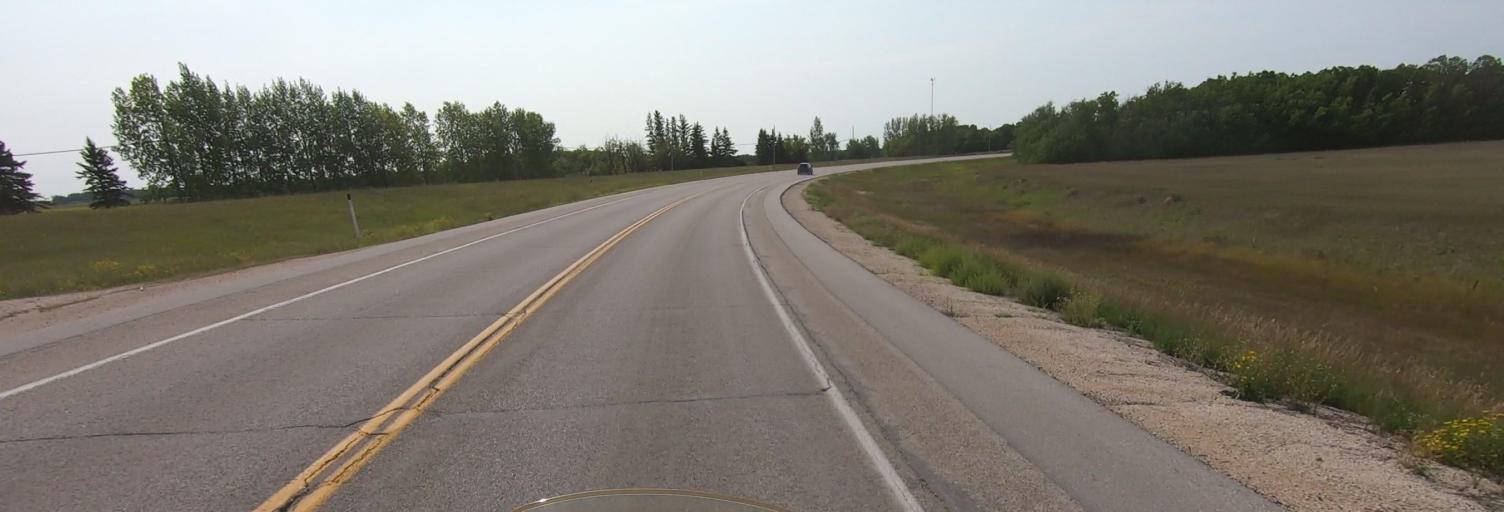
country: CA
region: Manitoba
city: Winnipeg
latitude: 49.7538
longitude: -97.1157
